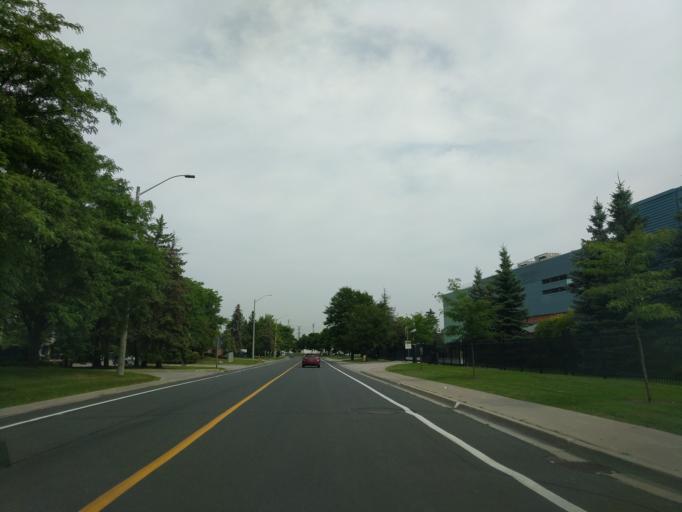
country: CA
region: Ontario
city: Markham
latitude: 43.8336
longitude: -79.3299
